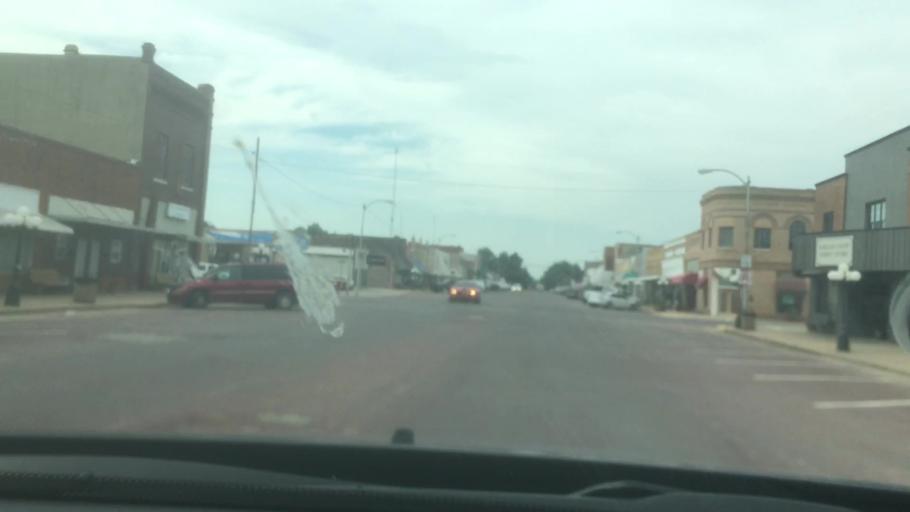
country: US
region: Oklahoma
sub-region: Garvin County
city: Lindsay
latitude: 34.8363
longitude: -97.6028
